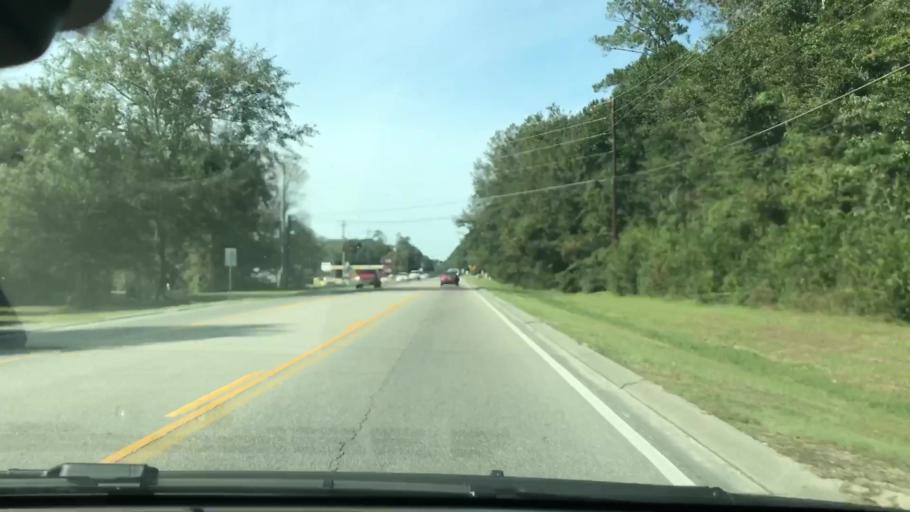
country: US
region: Louisiana
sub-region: Saint Tammany Parish
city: Pearl River
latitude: 30.3646
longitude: -89.7565
